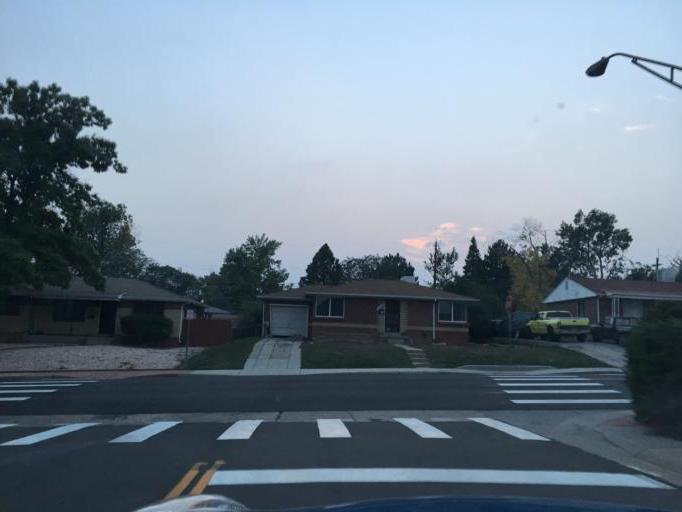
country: US
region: Colorado
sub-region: Arapahoe County
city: Sheridan
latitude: 39.6909
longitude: -105.0153
